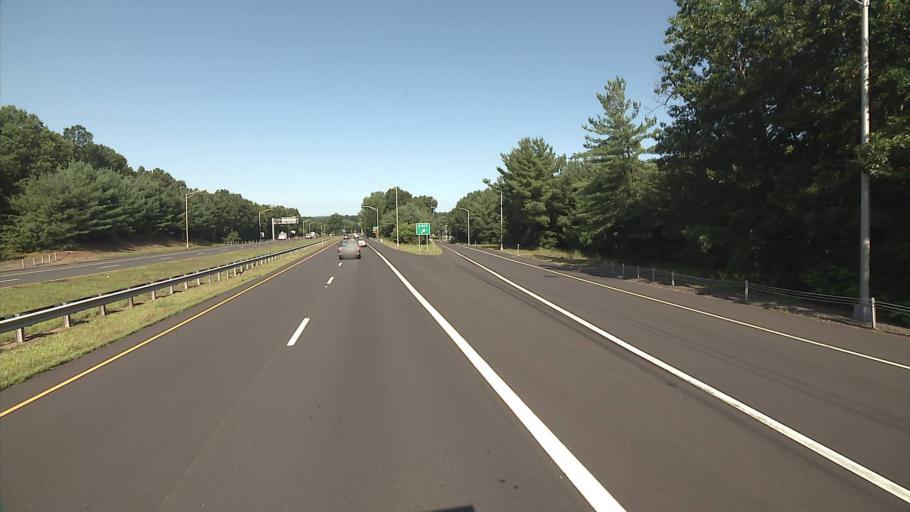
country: US
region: Connecticut
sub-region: Hartford County
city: Windsor Locks
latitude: 41.9177
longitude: -72.6804
